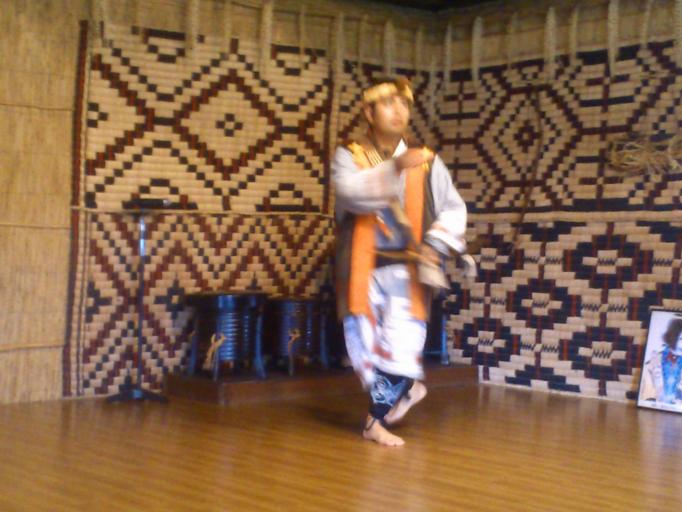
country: JP
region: Hokkaido
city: Shiraoi
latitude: 42.5595
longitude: 141.3665
